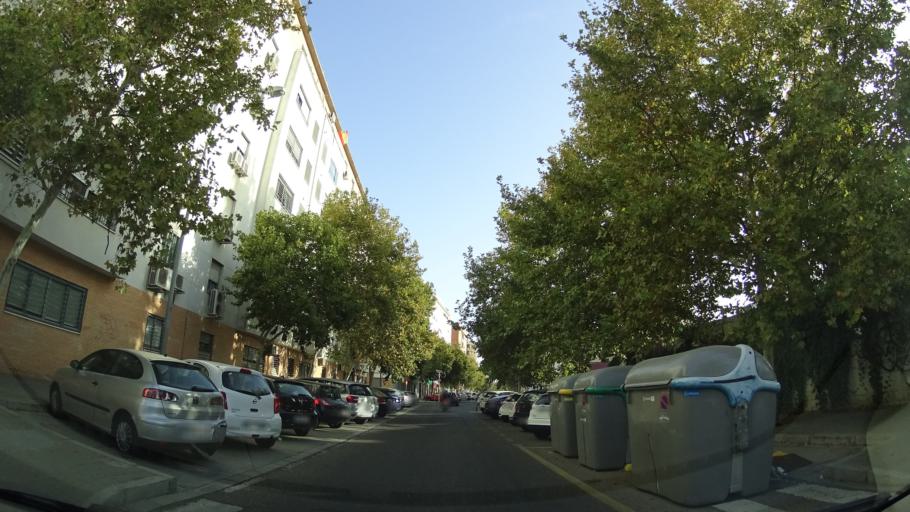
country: ES
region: Andalusia
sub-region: Provincia de Sevilla
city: Sevilla
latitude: 37.3974
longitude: -5.9714
